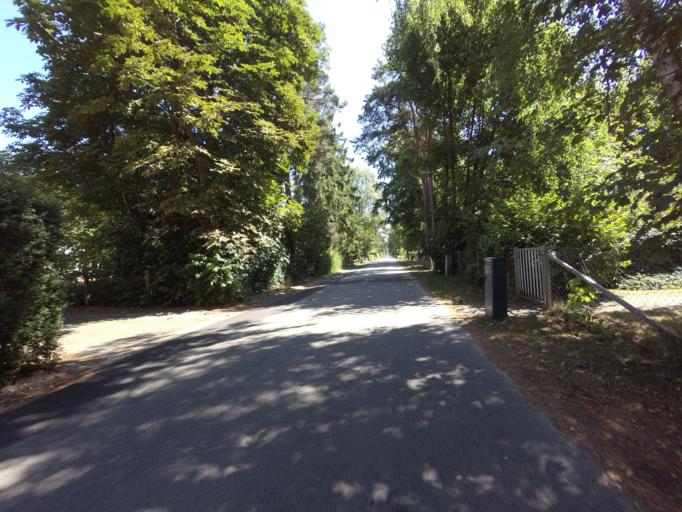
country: SE
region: Skane
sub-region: Vellinge Kommun
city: Ljunghusen
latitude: 55.4075
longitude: 12.9328
